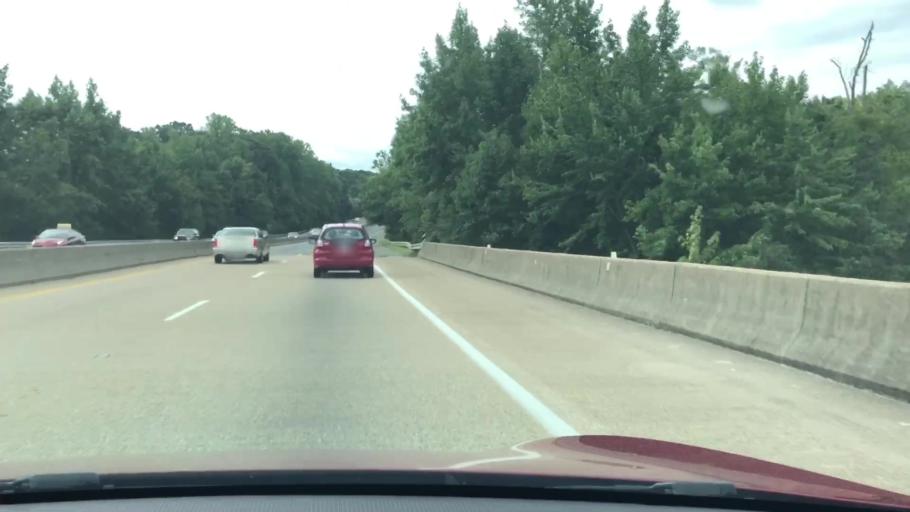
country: US
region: Virginia
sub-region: City of Chesapeake
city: Chesapeake
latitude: 36.7172
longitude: -76.2256
